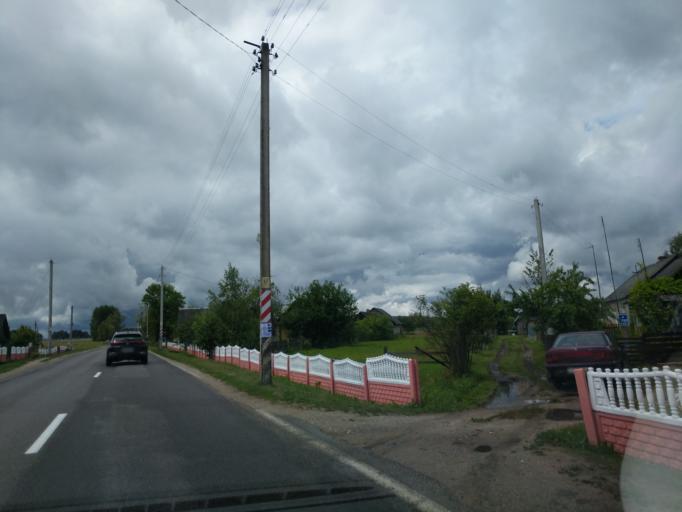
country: BY
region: Minsk
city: Il'ya
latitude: 54.4129
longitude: 27.2835
